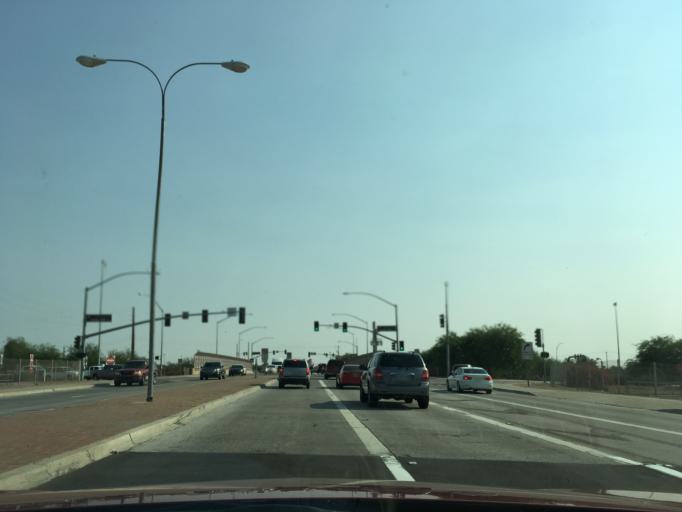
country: US
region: Arizona
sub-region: Maricopa County
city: Guadalupe
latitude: 33.2935
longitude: -111.9457
